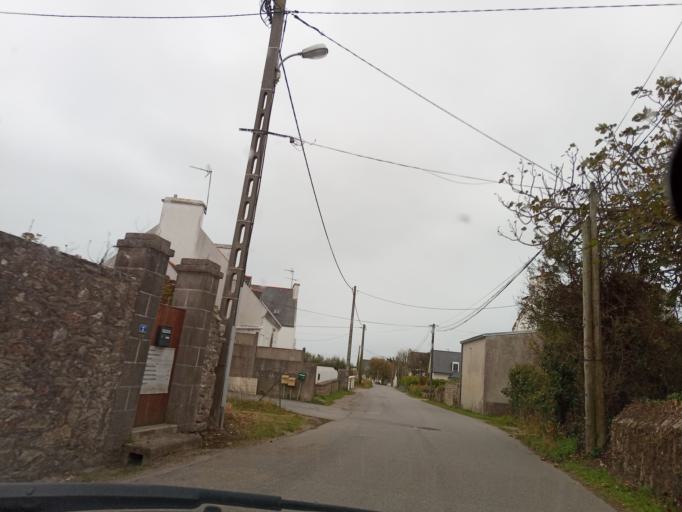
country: FR
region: Brittany
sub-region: Departement du Finistere
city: Esquibien
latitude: 48.0211
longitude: -4.5637
